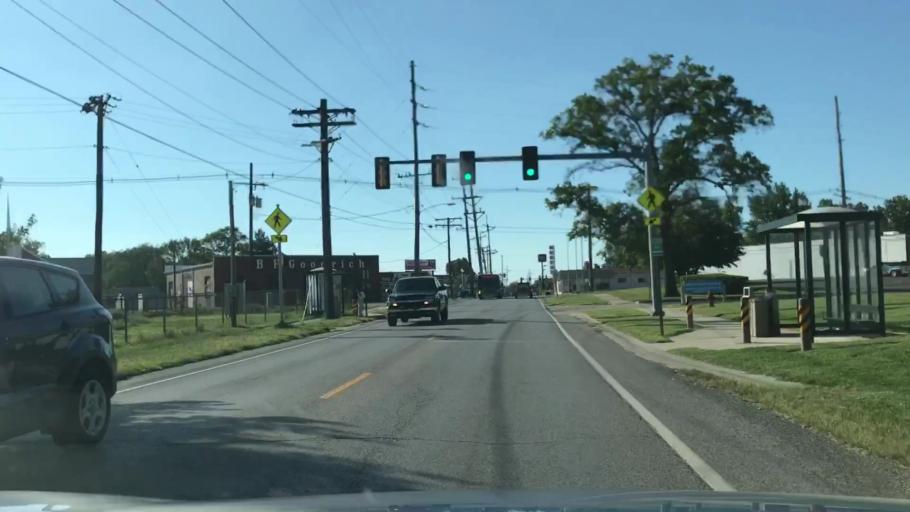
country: US
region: Illinois
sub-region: Madison County
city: Wood River
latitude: 38.8726
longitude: -90.0962
